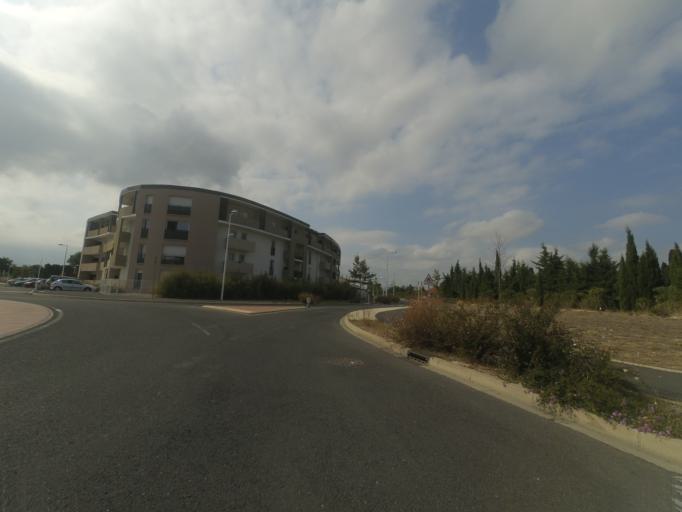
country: FR
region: Languedoc-Roussillon
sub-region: Departement des Pyrenees-Orientales
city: Le Soler
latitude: 42.6795
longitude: 2.8076
